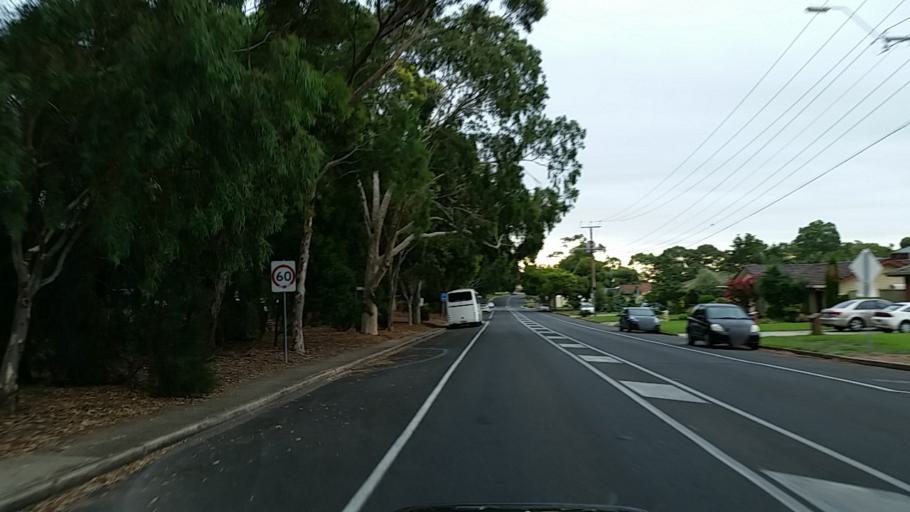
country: AU
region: South Australia
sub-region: Campbelltown
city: Athelstone
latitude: -34.8674
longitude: 138.6931
